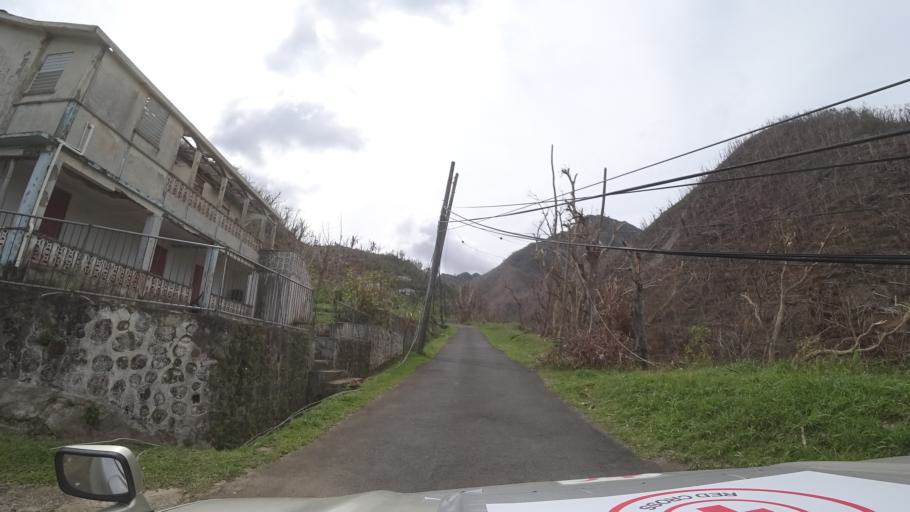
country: DM
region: Saint Patrick
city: Berekua
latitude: 15.2367
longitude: -61.3269
